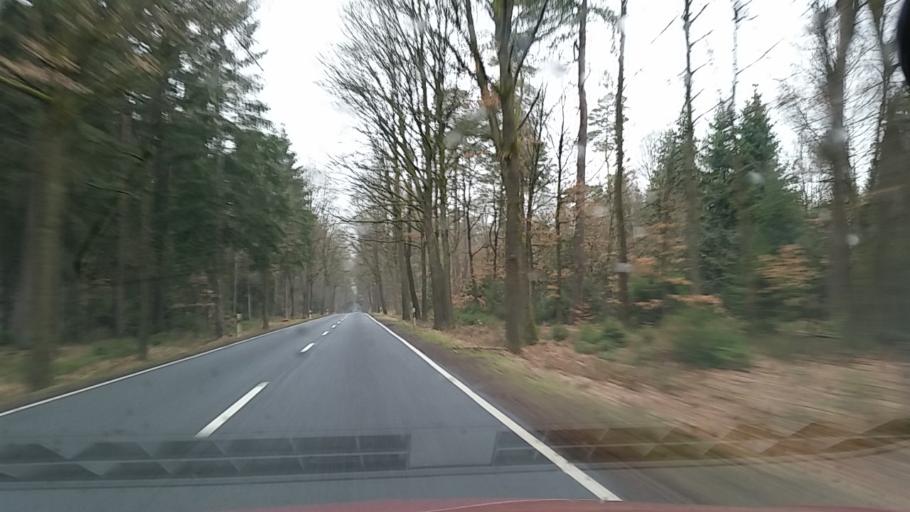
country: DE
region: Lower Saxony
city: Sprakensehl
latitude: 52.7800
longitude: 10.4257
